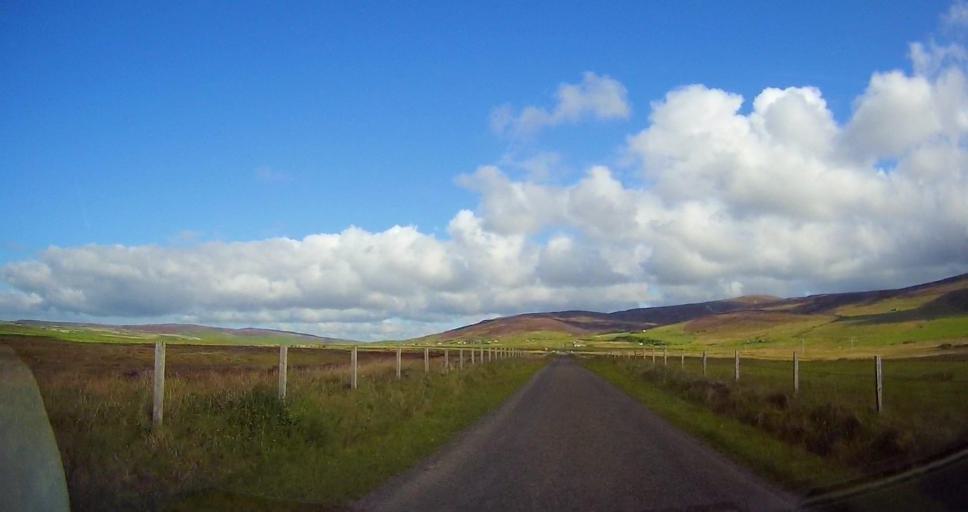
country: GB
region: Scotland
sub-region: Orkney Islands
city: Stromness
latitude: 58.9843
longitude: -3.1878
